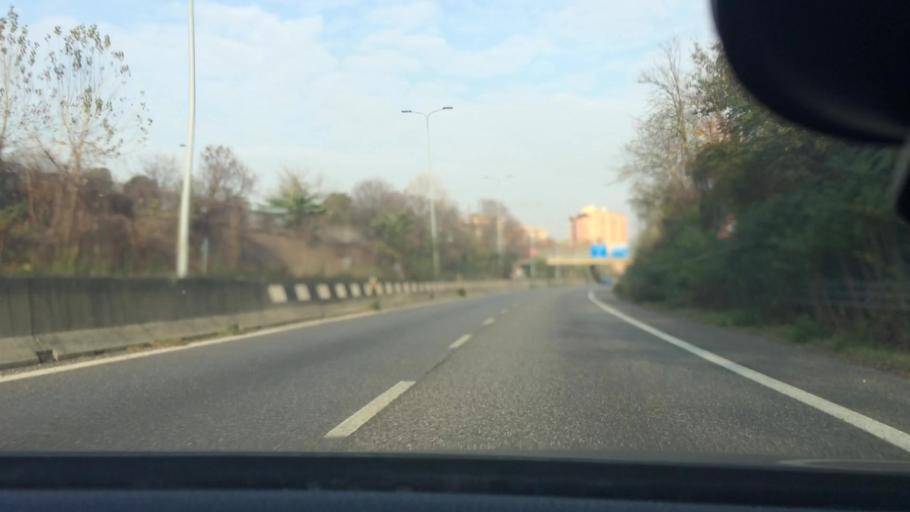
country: IT
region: Lombardy
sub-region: Citta metropolitana di Milano
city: Cormano
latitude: 45.5422
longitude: 9.1618
